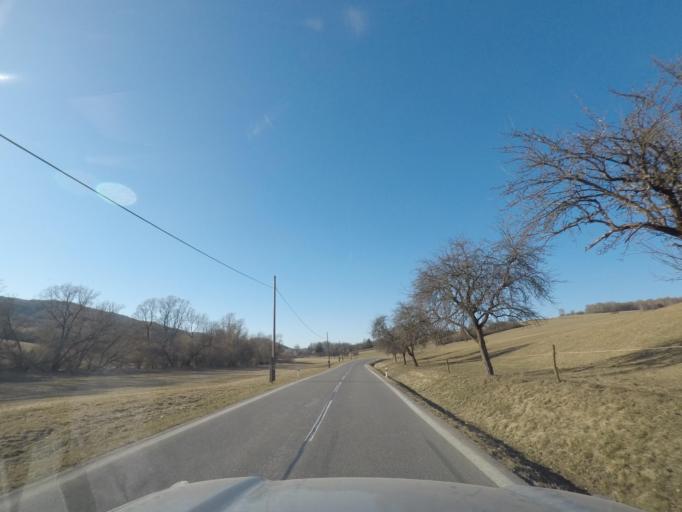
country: SK
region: Presovsky
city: Medzilaborce
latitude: 49.1856
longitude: 22.0127
